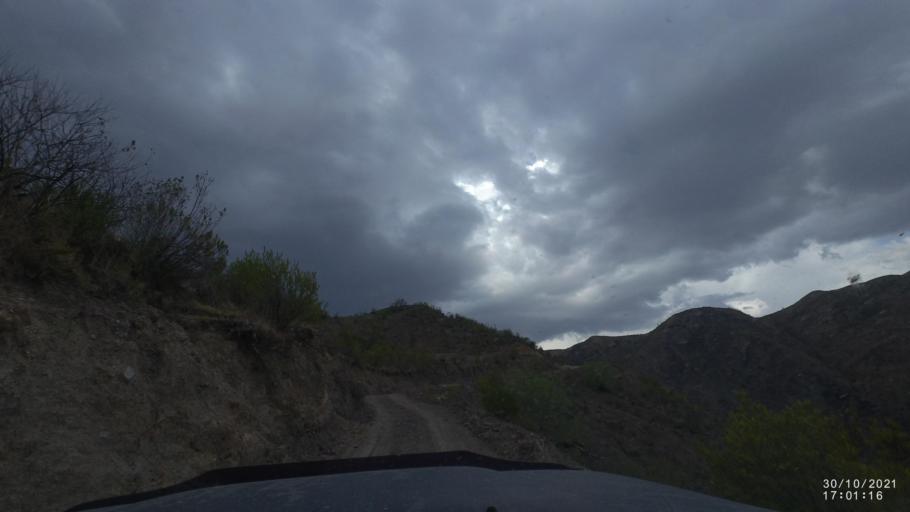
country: BO
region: Cochabamba
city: Colchani
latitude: -17.5719
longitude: -66.6318
